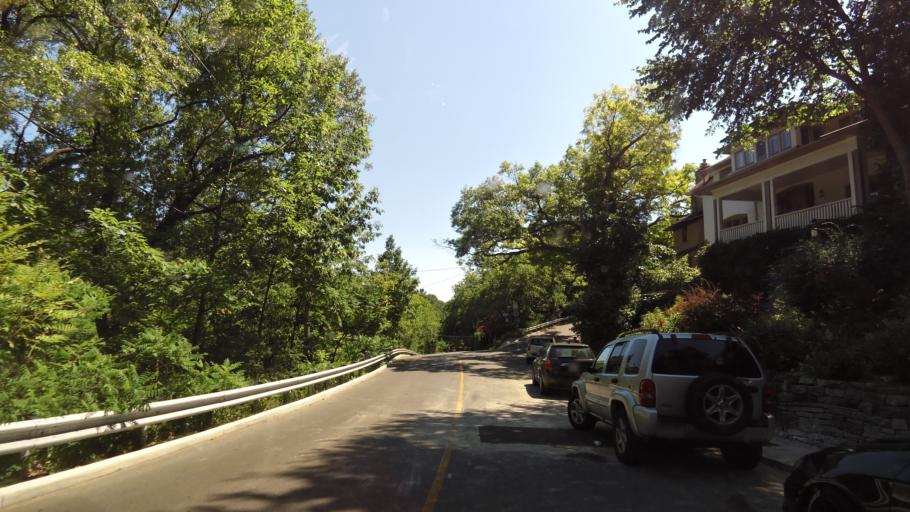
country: CA
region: Ontario
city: Toronto
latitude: 43.6515
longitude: -79.4709
